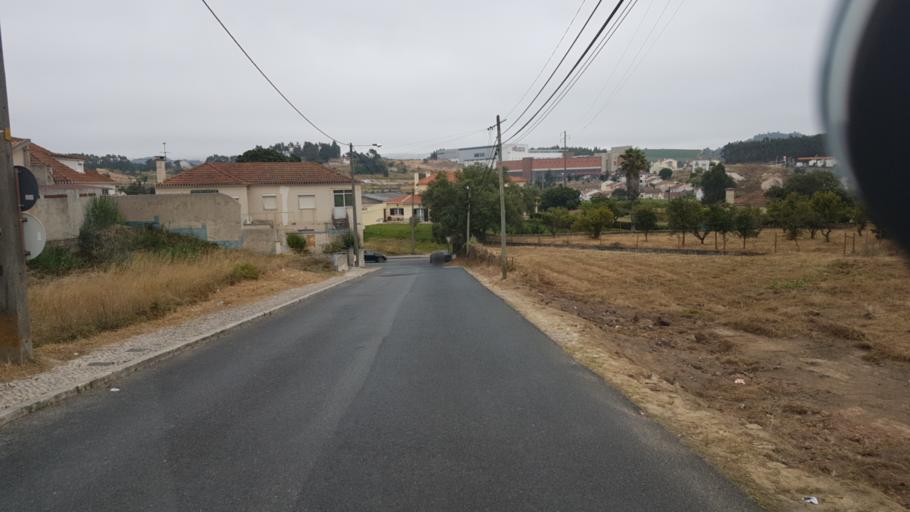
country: PT
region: Lisbon
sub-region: Torres Vedras
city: Torres Vedras
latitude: 39.1037
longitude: -9.2605
